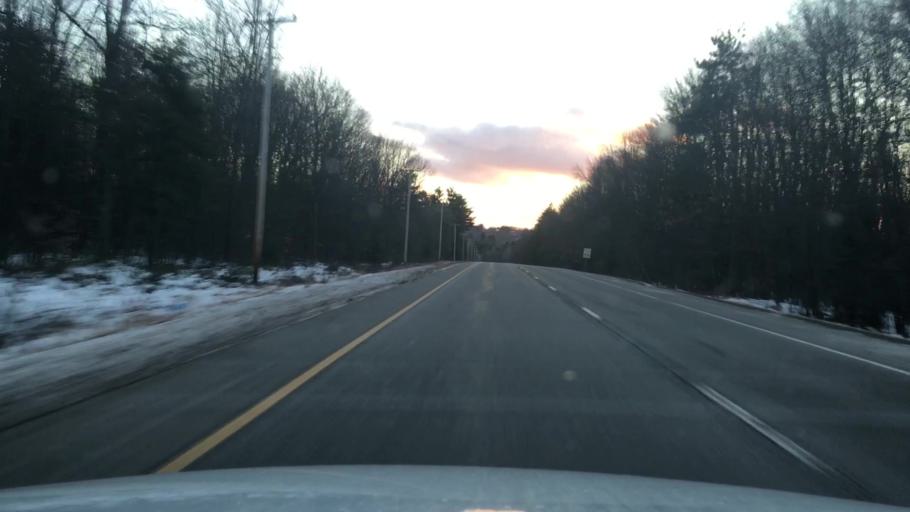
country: US
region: Maine
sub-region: Androscoggin County
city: Auburn
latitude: 44.0667
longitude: -70.2502
